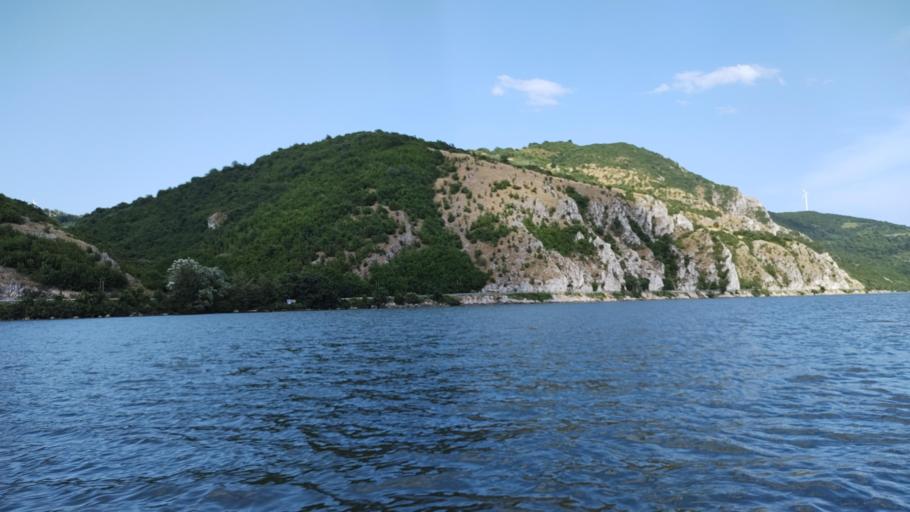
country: RO
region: Caras-Severin
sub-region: Comuna Pescari
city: Coronini
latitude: 44.6667
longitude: 21.6887
